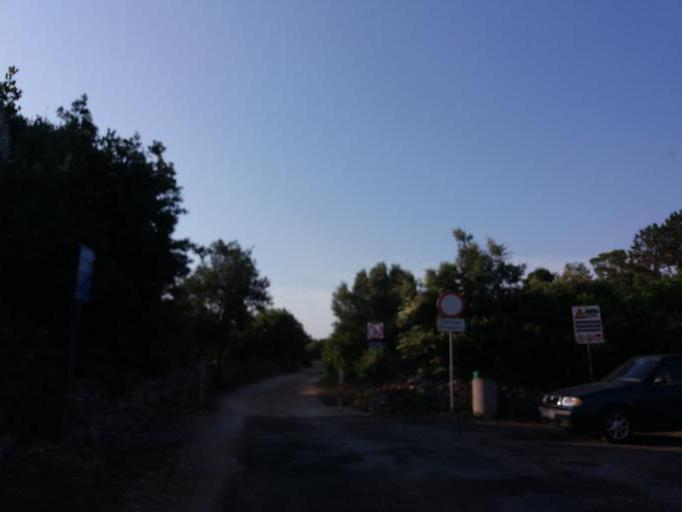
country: HR
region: Zadarska
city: Sali
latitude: 43.9036
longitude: 15.1440
